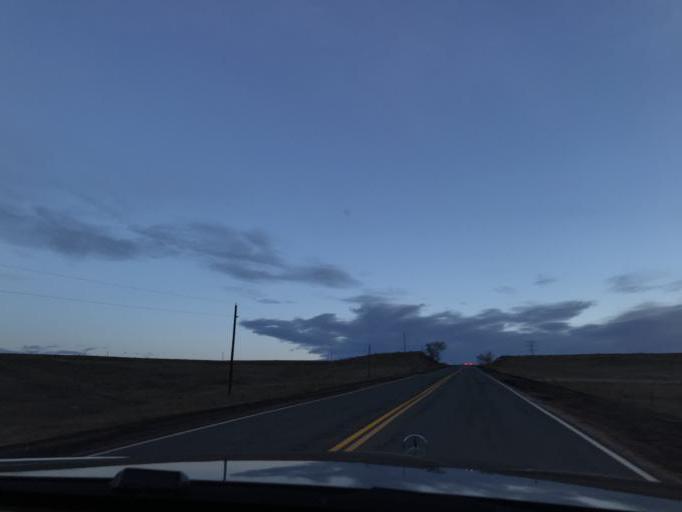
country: US
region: Colorado
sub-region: Boulder County
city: Superior
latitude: 39.9054
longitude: -105.1656
